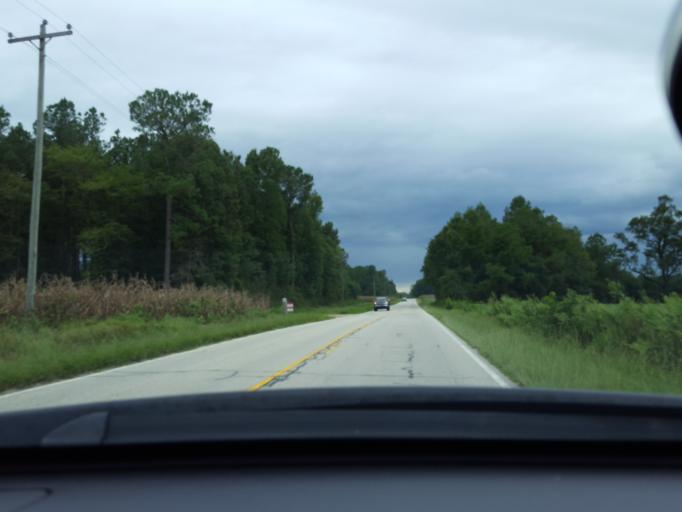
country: US
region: North Carolina
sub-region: Duplin County
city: Rose Hill
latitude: 34.8123
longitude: -78.1878
